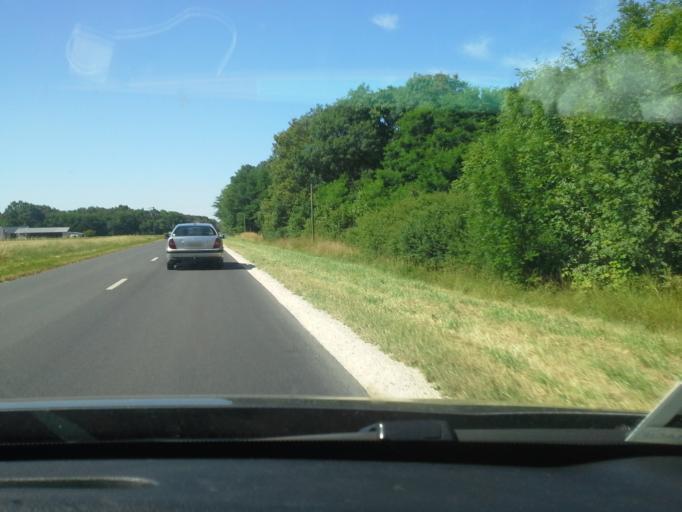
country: FR
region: Centre
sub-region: Departement du Loir-et-Cher
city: Cormeray
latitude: 47.5051
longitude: 1.4047
